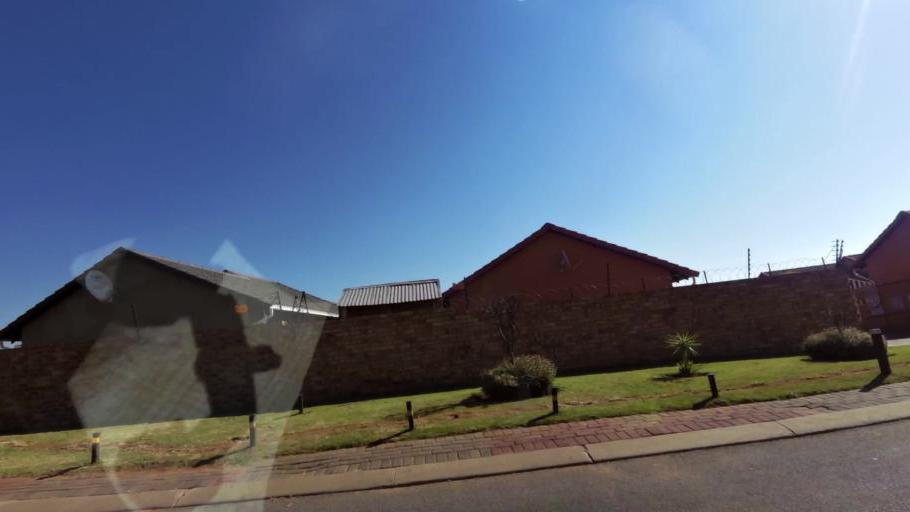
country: ZA
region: Gauteng
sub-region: City of Johannesburg Metropolitan Municipality
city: Johannesburg
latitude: -26.2411
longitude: 28.0001
